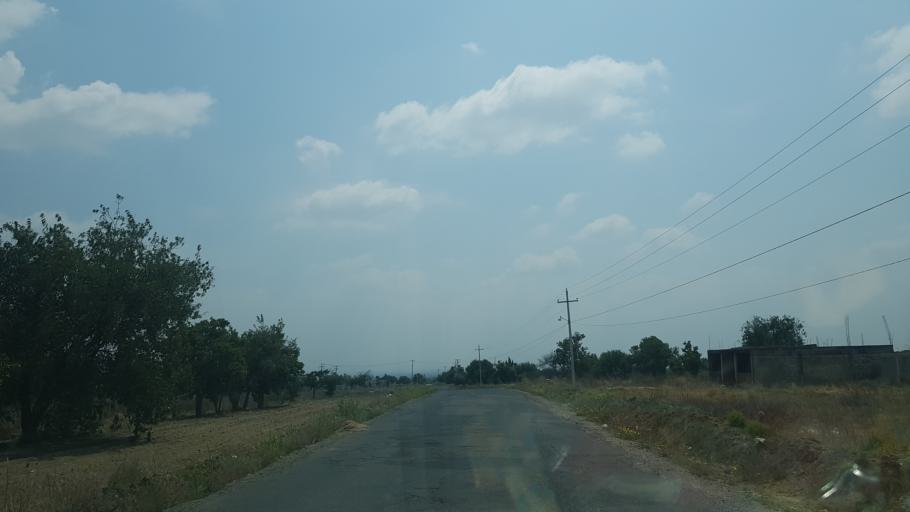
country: MX
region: Puebla
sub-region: Huejotzingo
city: San Juan Pancoac
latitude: 19.1375
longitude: -98.4233
